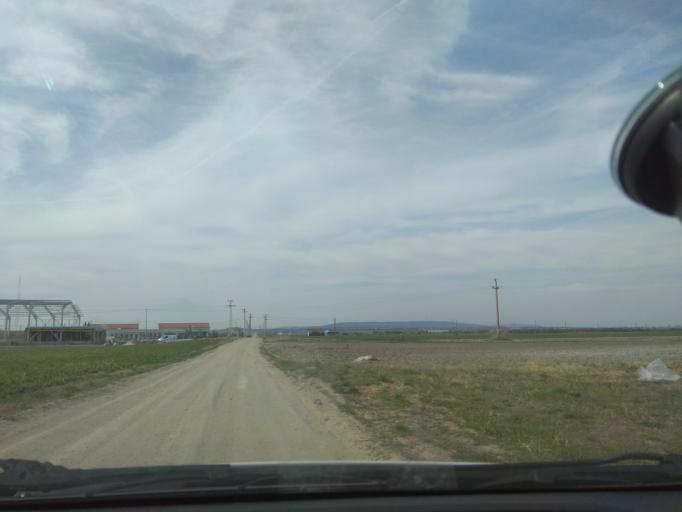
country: HU
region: Pest
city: Szigetszentmiklos
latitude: 47.3594
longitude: 19.0351
